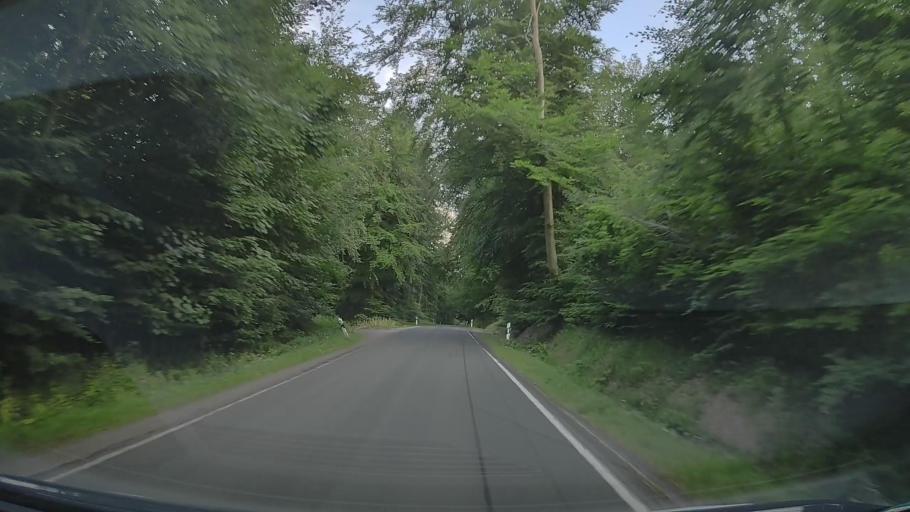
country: DE
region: North Rhine-Westphalia
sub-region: Regierungsbezirk Detmold
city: Barntrup
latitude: 51.9501
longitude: 9.1397
